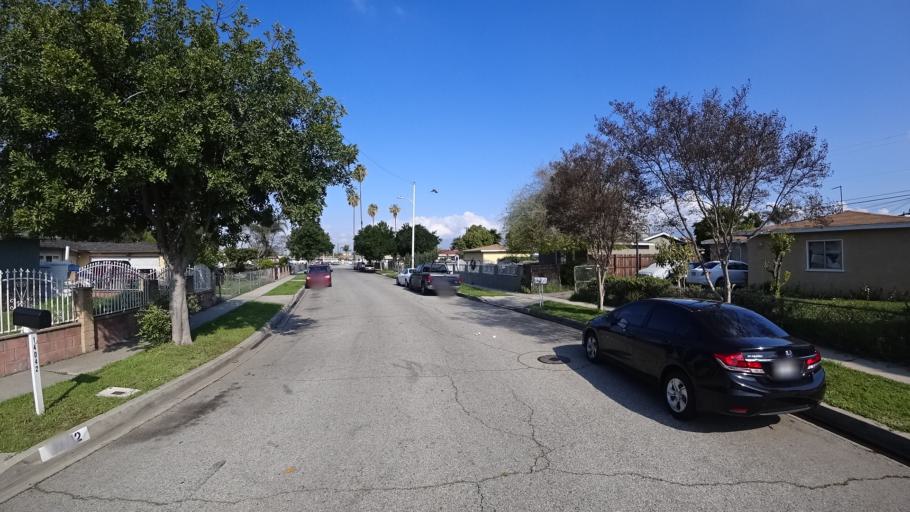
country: US
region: California
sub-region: Los Angeles County
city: Baldwin Park
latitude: 34.0720
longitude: -117.9703
